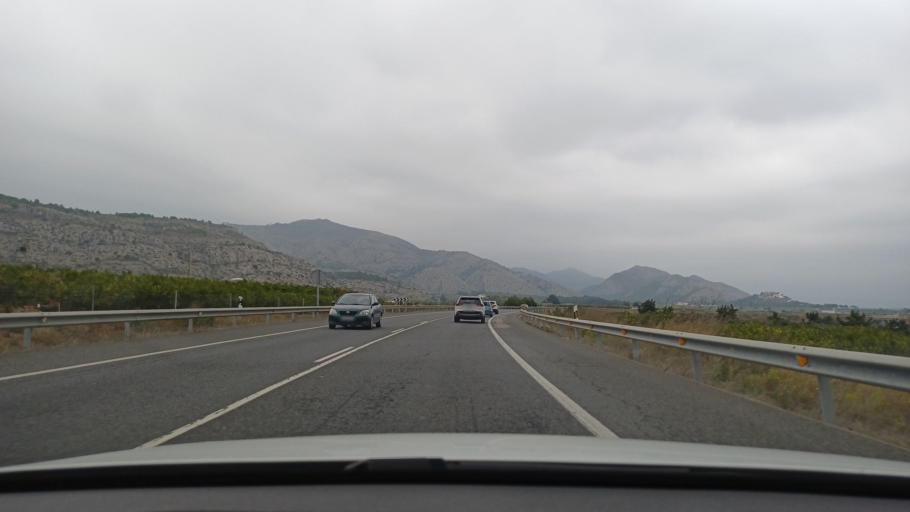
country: ES
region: Valencia
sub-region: Provincia de Castello
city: Borriol
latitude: 40.0264
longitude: -0.0341
